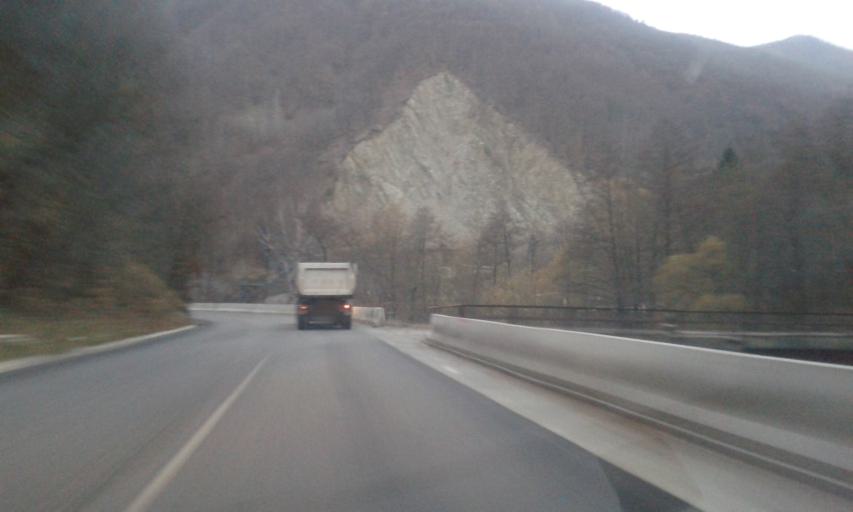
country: RO
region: Gorj
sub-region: Comuna Bumbesti-Jiu
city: Bumbesti-Jiu
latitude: 45.2178
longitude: 23.3781
